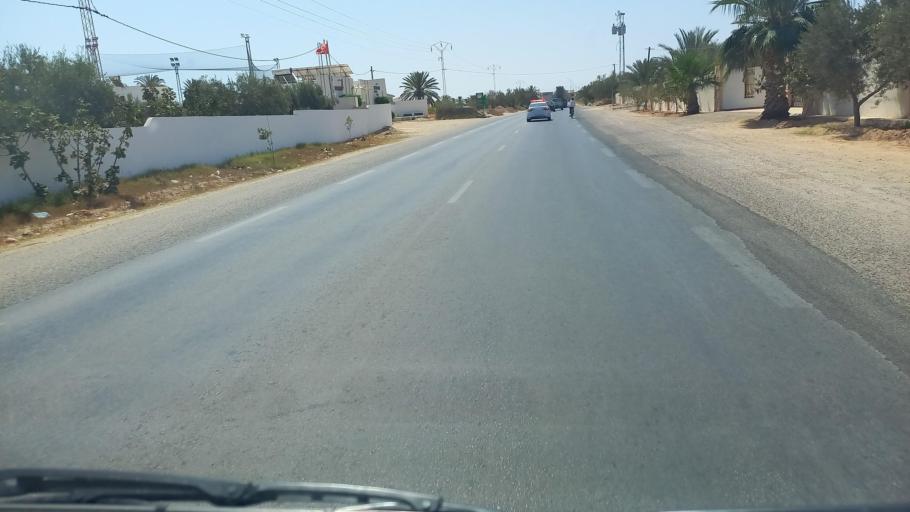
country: TN
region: Madanin
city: Houmt Souk
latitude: 33.7909
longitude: 10.8877
